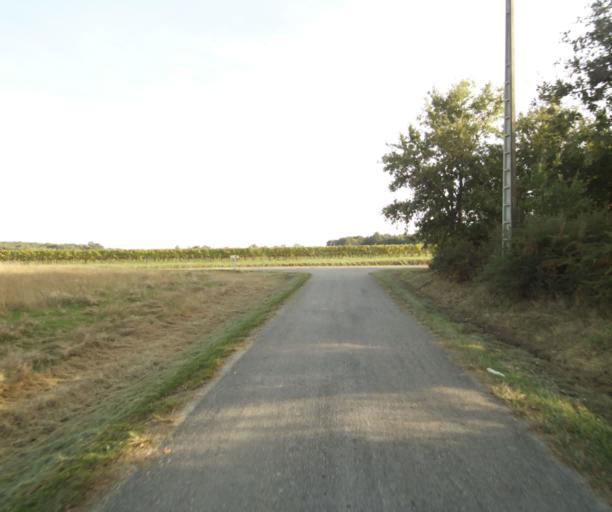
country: FR
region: Midi-Pyrenees
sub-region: Departement du Tarn-et-Garonne
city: Campsas
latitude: 43.8995
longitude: 1.3421
